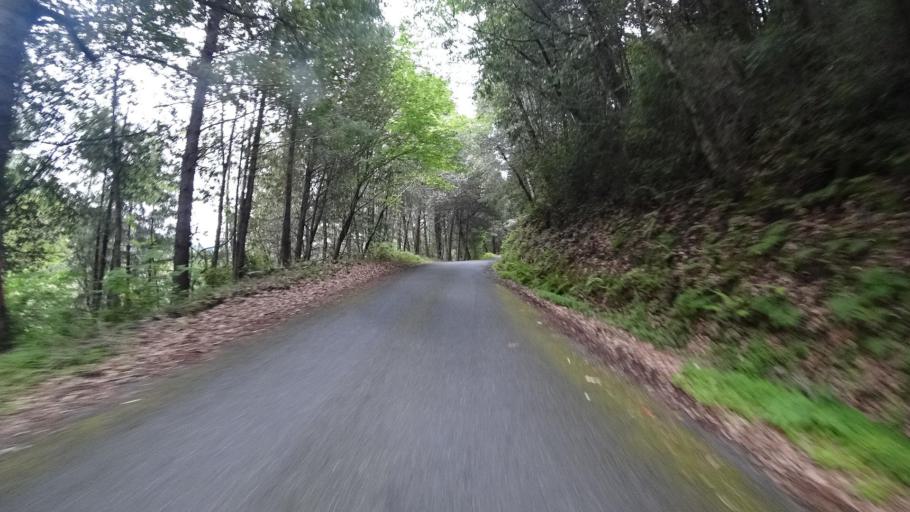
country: US
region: California
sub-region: Humboldt County
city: Willow Creek
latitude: 41.2021
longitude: -123.7557
